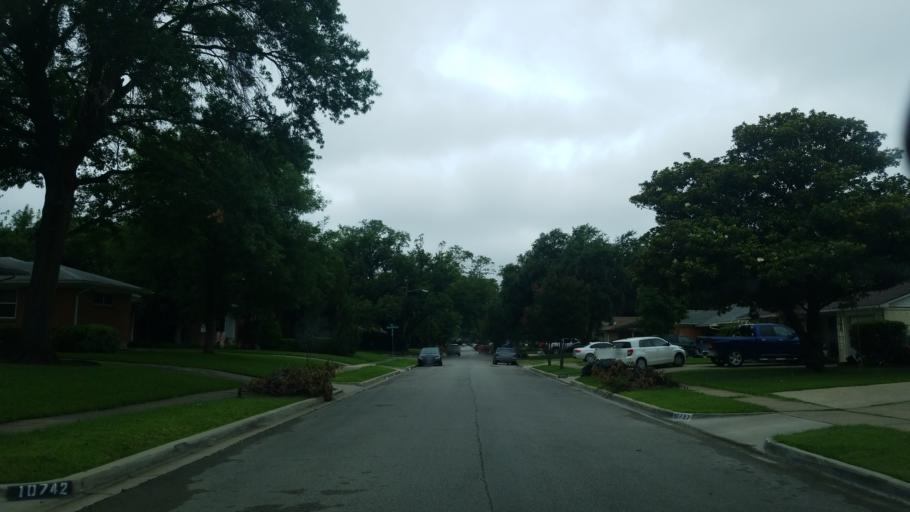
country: US
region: Texas
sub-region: Dallas County
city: Farmers Branch
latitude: 32.8941
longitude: -96.8761
